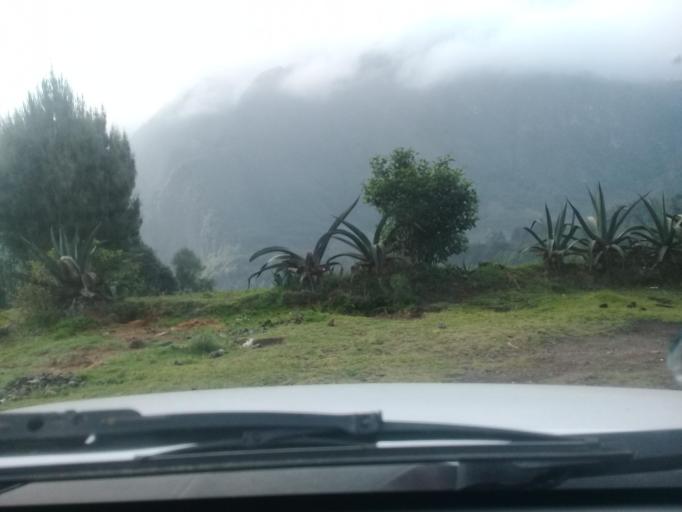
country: MX
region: Veracruz
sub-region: Mariano Escobedo
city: San Isidro el Berro
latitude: 18.9504
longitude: -97.1995
